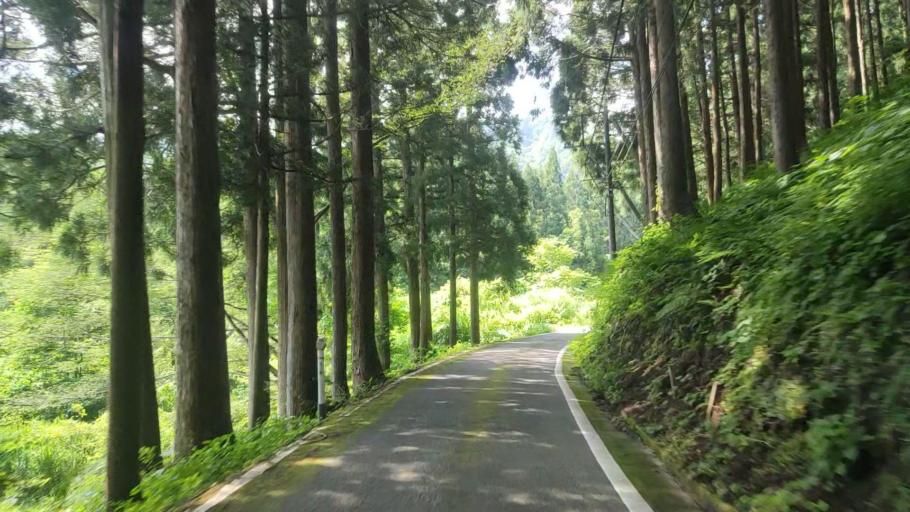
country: JP
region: Ishikawa
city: Komatsu
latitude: 36.2531
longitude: 136.5397
